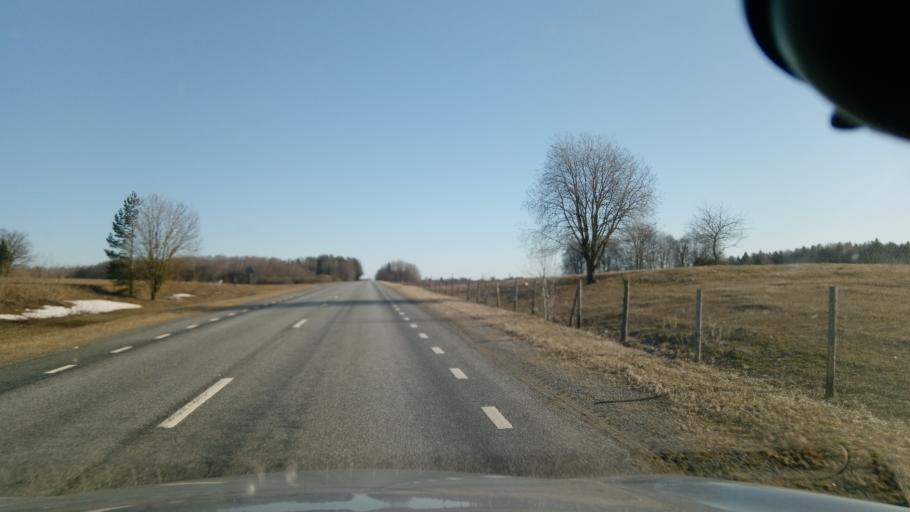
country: EE
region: Jaervamaa
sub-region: Jaerva-Jaani vald
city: Jarva-Jaani
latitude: 59.0833
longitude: 25.9667
